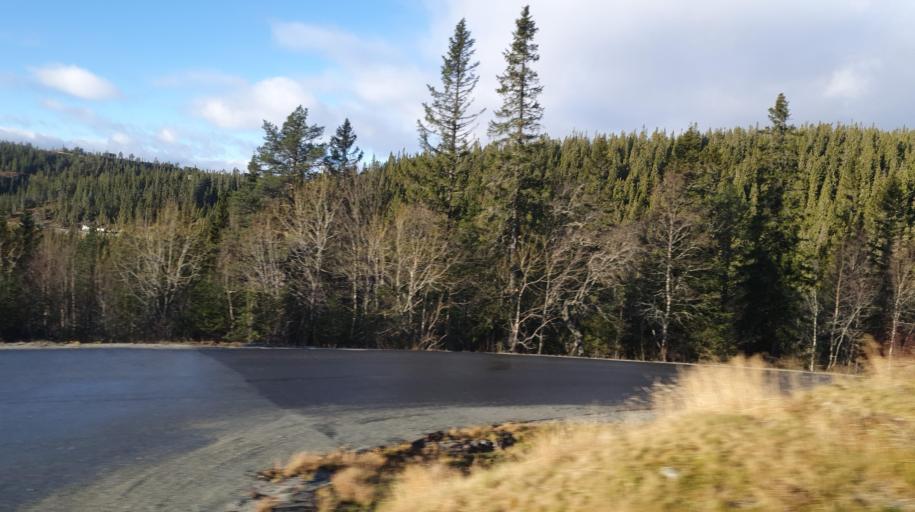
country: NO
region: Buskerud
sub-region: Krodsherad
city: Noresund
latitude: 60.2194
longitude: 9.5338
